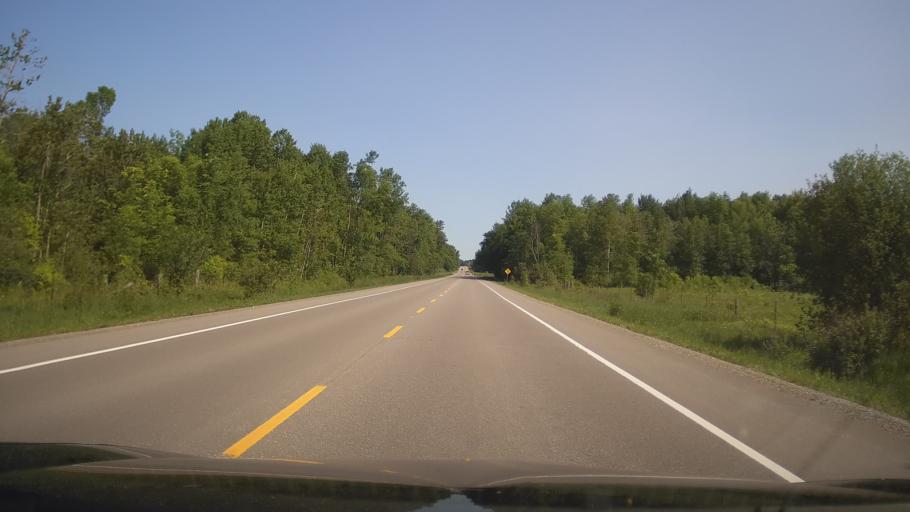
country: CA
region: Ontario
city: Omemee
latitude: 44.3777
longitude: -78.8995
